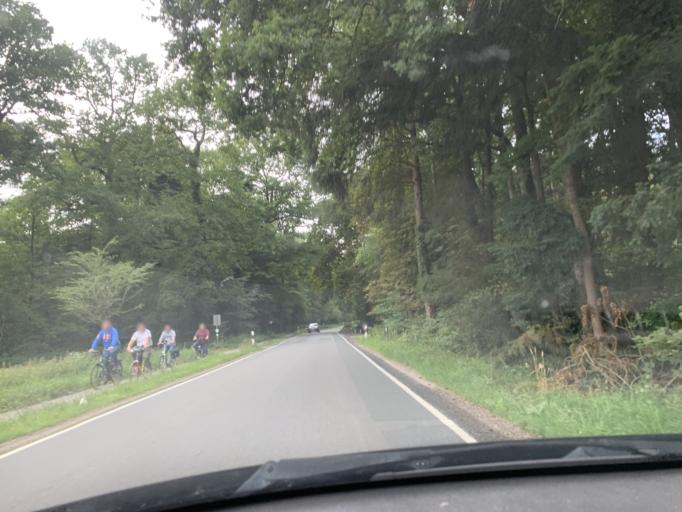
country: DE
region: Lower Saxony
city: Westerstede
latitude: 53.2715
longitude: 7.9413
